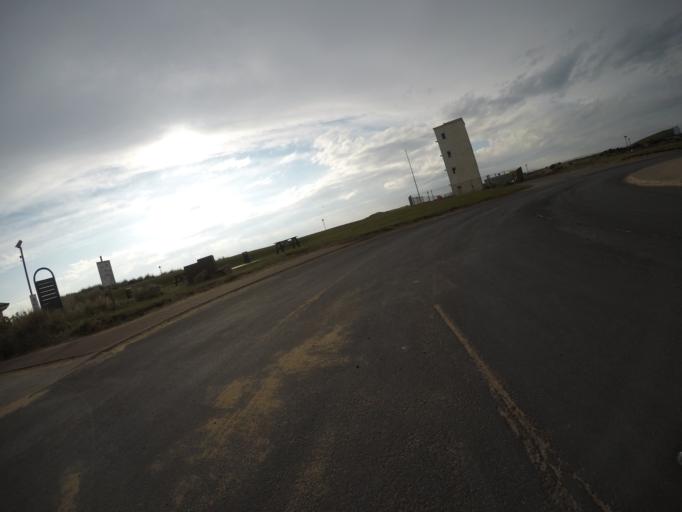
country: GB
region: Scotland
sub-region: North Ayrshire
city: Irvine
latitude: 55.6053
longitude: -4.6935
